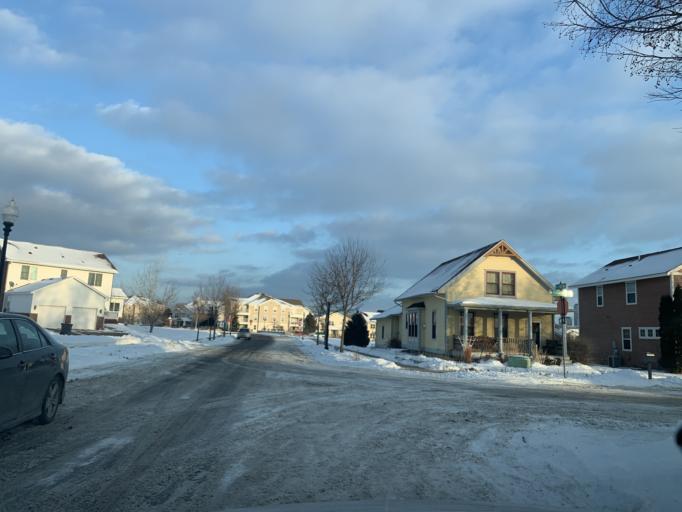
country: US
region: Minnesota
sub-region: Hennepin County
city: Minneapolis
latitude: 44.9890
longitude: -93.2943
